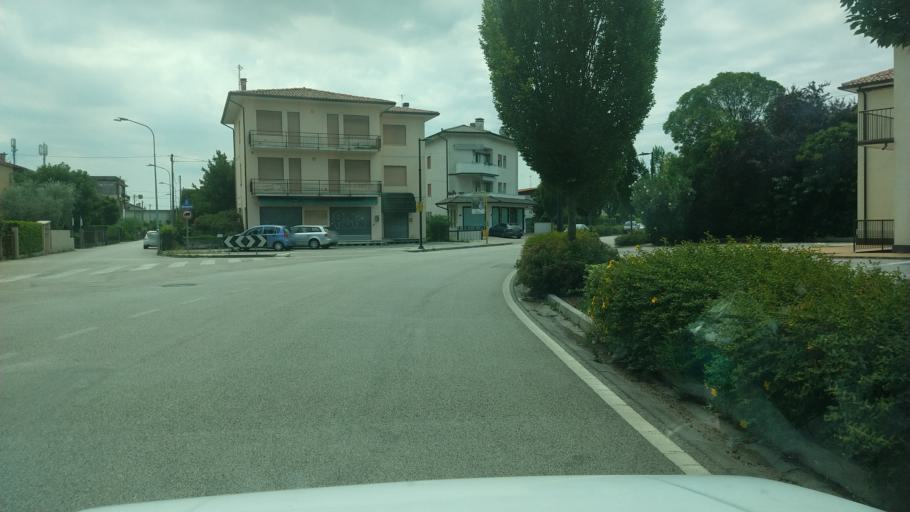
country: IT
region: Veneto
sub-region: Provincia di Vicenza
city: Romano d'Ezzelino
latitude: 45.7734
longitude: 11.7565
